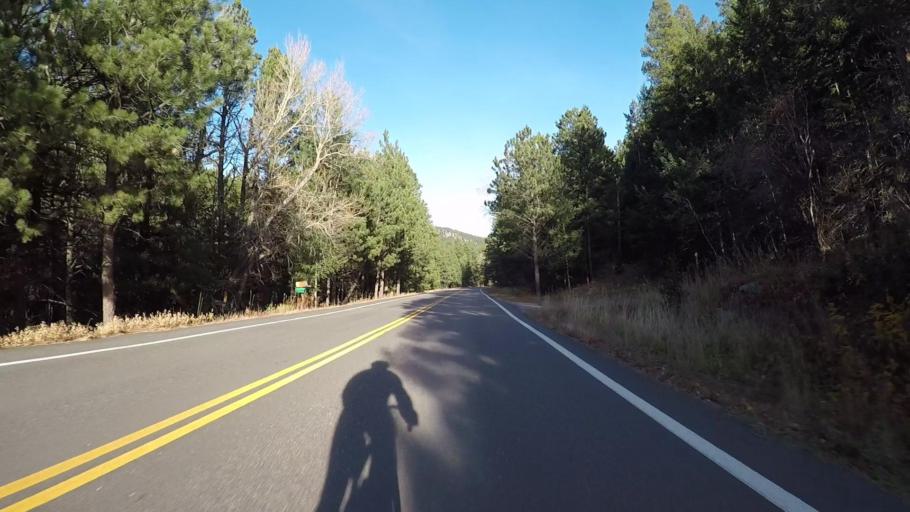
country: US
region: Colorado
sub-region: Boulder County
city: Boulder
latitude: 40.0898
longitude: -105.3611
